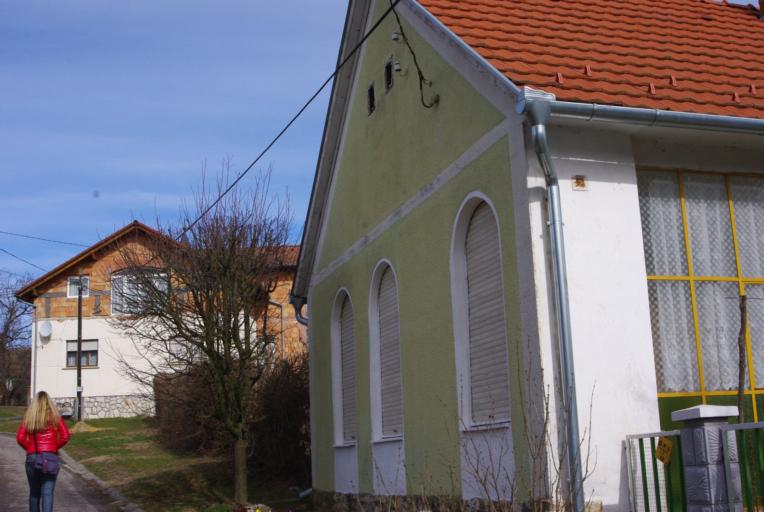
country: HU
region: Baranya
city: Villany
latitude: 45.8813
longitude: 18.4248
